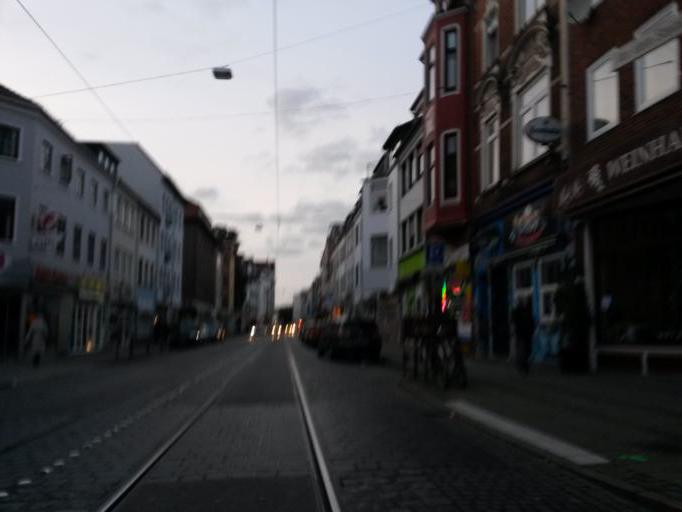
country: DE
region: Bremen
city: Bremen
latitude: 53.0715
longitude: 8.8310
